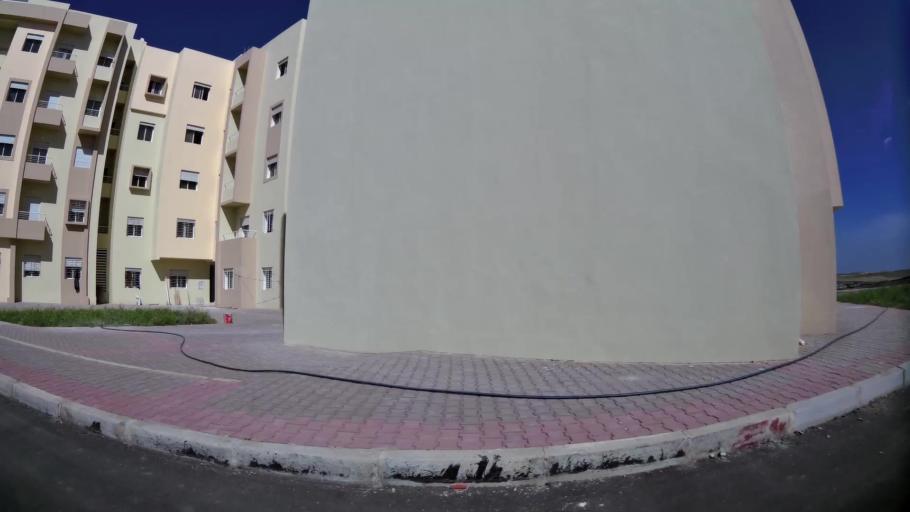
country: MA
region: Oriental
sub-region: Oujda-Angad
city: Oujda
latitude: 34.6504
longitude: -1.9545
